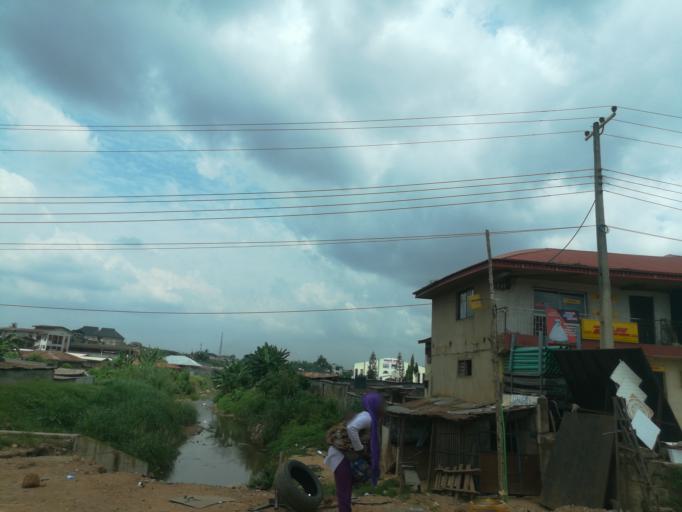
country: NG
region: Oyo
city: Ibadan
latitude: 7.4032
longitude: 3.9391
